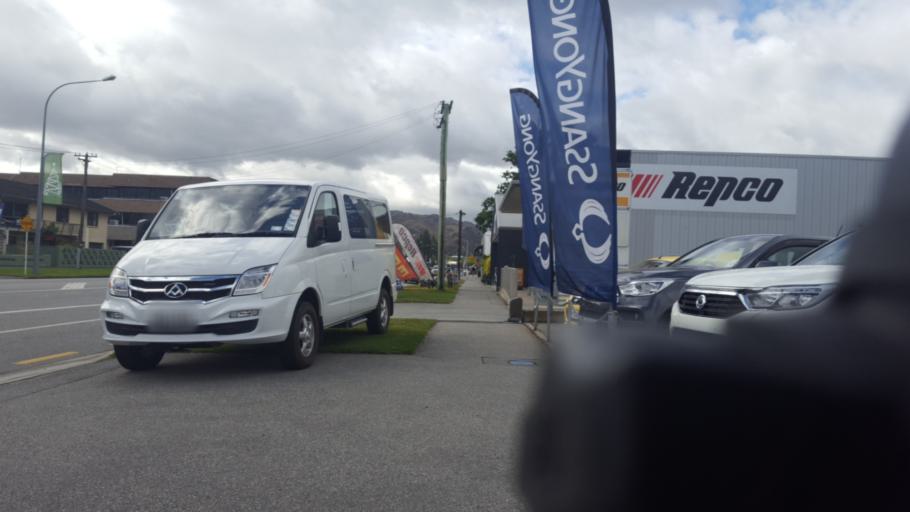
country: NZ
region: Otago
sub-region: Queenstown-Lakes District
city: Wanaka
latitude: -45.2502
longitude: 169.3866
